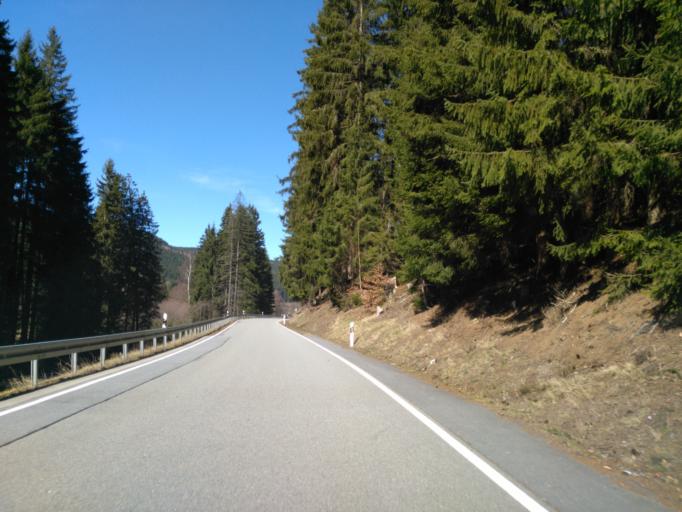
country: DE
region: Saxony
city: Rittersgrun
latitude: 50.4582
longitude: 12.8255
